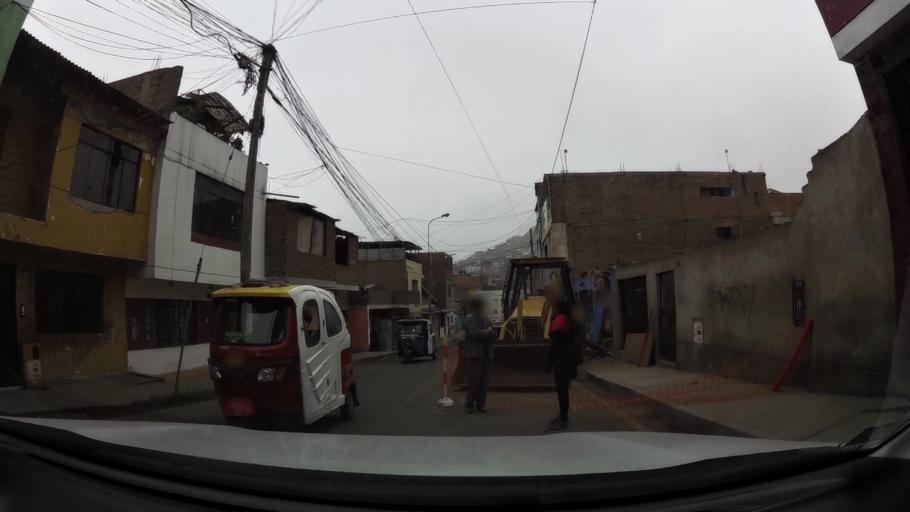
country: PE
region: Lima
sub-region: Lima
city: Surco
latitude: -12.1562
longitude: -76.9542
